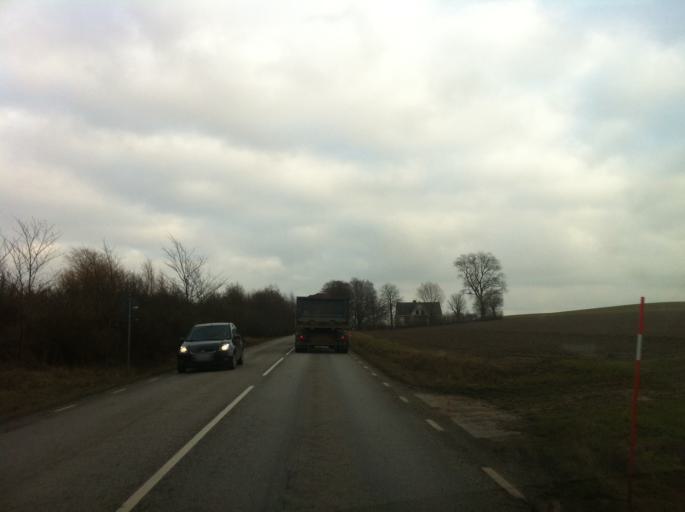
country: SE
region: Skane
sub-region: Kavlinge Kommun
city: Loddekopinge
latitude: 55.8187
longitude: 13.0329
